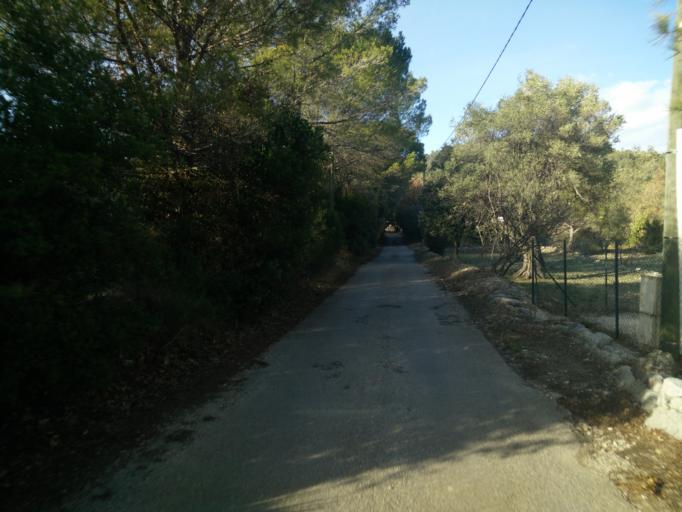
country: FR
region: Provence-Alpes-Cote d'Azur
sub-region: Departement du Var
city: Sollies-Toucas
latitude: 43.2044
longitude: 5.9830
